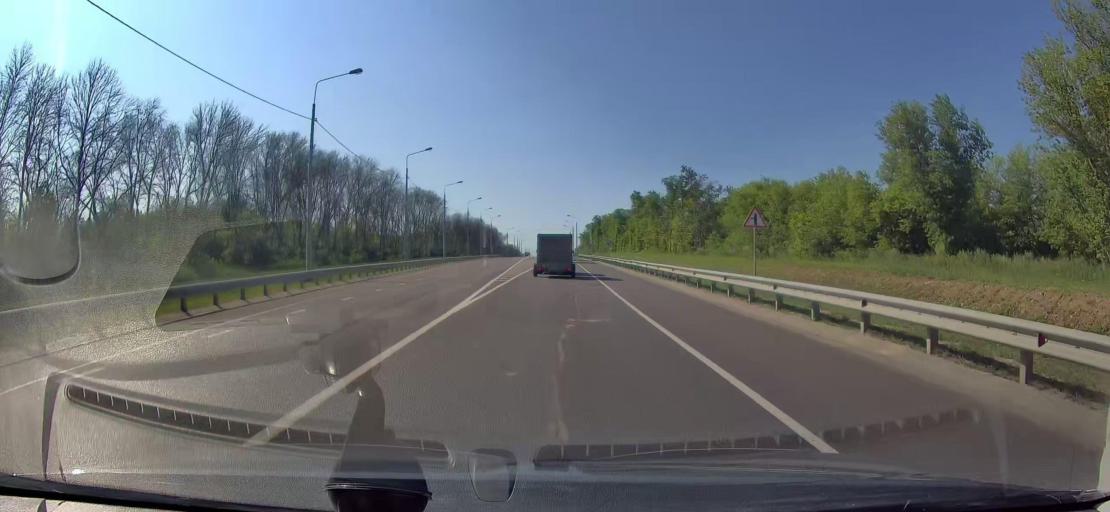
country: RU
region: Orjol
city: Kromy
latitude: 52.6343
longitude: 35.7517
